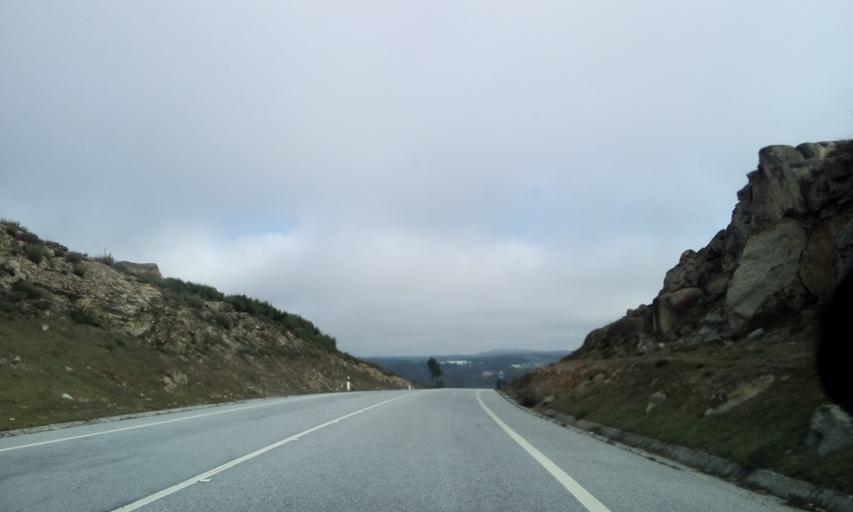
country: PT
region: Guarda
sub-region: Aguiar da Beira
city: Aguiar da Beira
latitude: 40.7677
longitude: -7.5030
